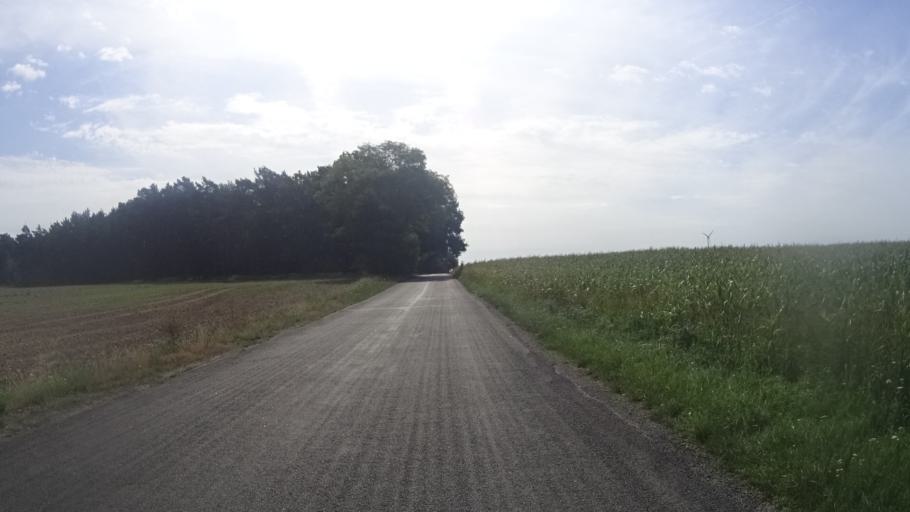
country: DE
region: Brandenburg
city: Golzow
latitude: 52.3198
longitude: 12.6819
